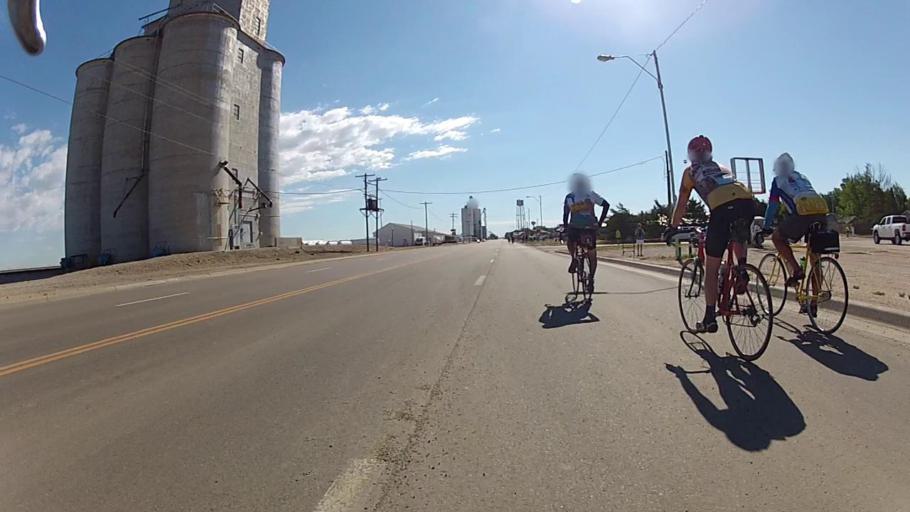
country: US
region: Kansas
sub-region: Gray County
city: Cimarron
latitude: 37.5973
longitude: -100.4491
